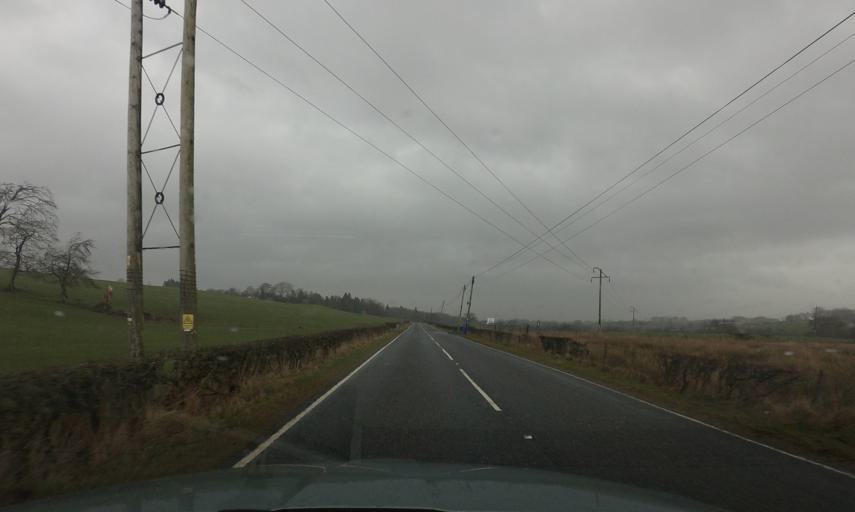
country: GB
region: Scotland
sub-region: Stirling
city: Balfron
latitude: 56.0928
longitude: -4.3629
